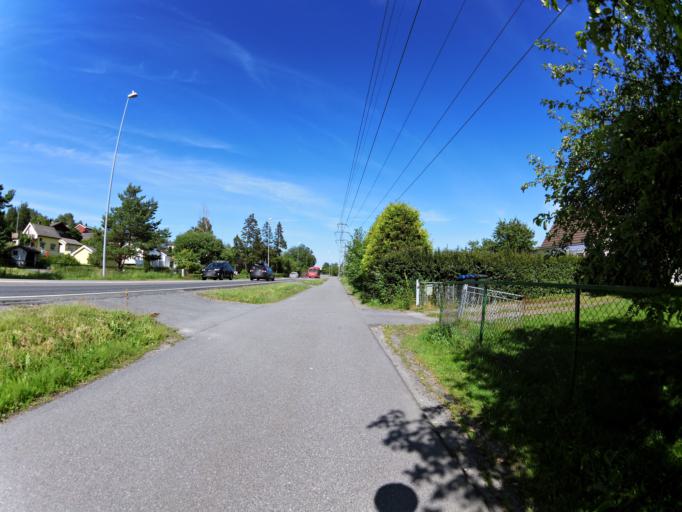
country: NO
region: Ostfold
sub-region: Fredrikstad
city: Fredrikstad
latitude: 59.2459
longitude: 10.9847
